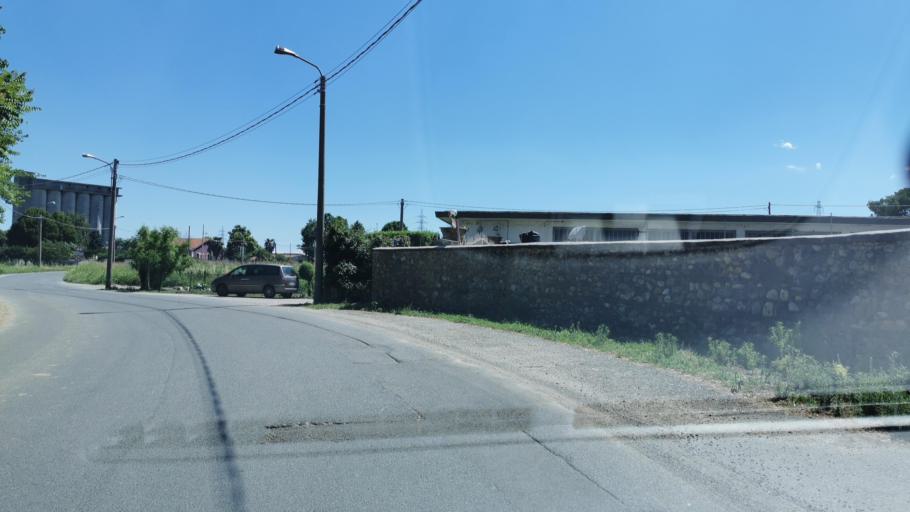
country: IT
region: Piedmont
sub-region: Provincia di Torino
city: Druento
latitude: 45.1187
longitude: 7.5629
